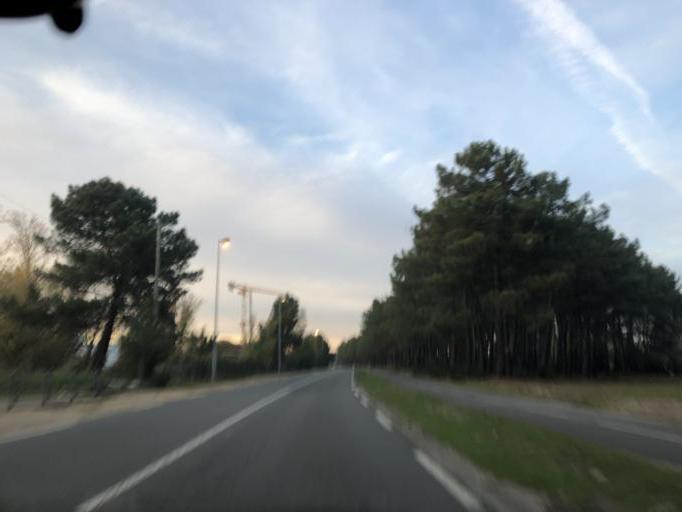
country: FR
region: Aquitaine
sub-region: Departement de la Gironde
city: Le Bouscat
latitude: 44.8808
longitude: -0.5838
